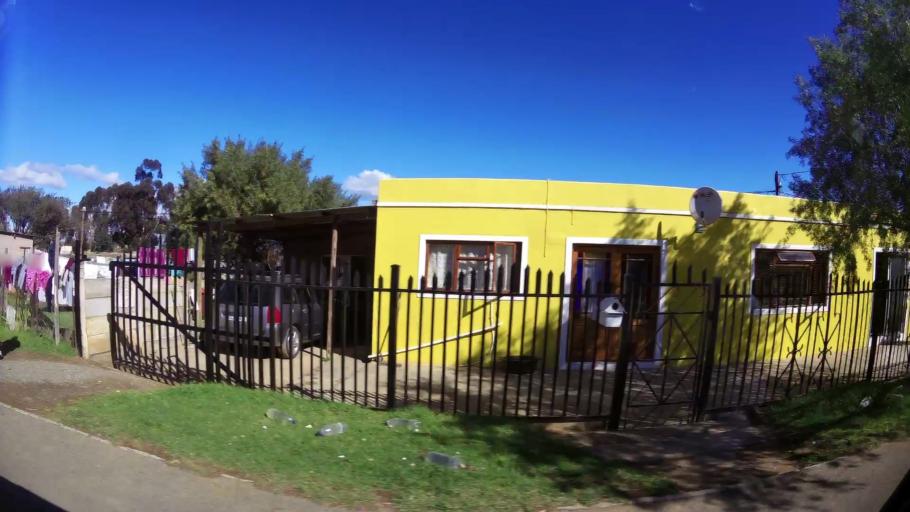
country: ZA
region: Western Cape
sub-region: Cape Winelands District Municipality
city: Ashton
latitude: -33.7931
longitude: 19.8808
